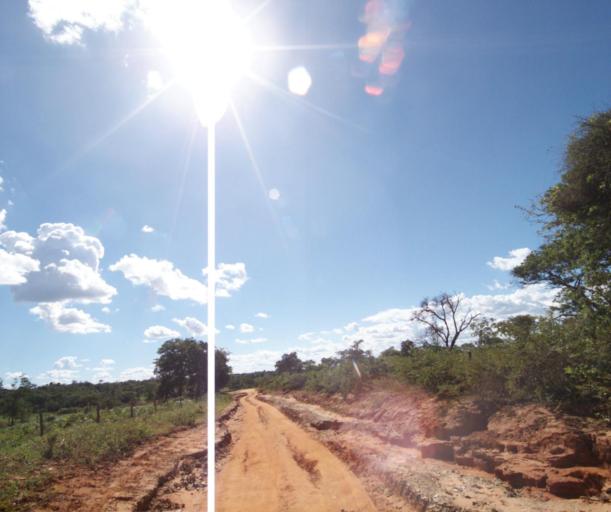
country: BR
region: Bahia
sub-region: Carinhanha
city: Carinhanha
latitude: -14.1873
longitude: -44.4918
